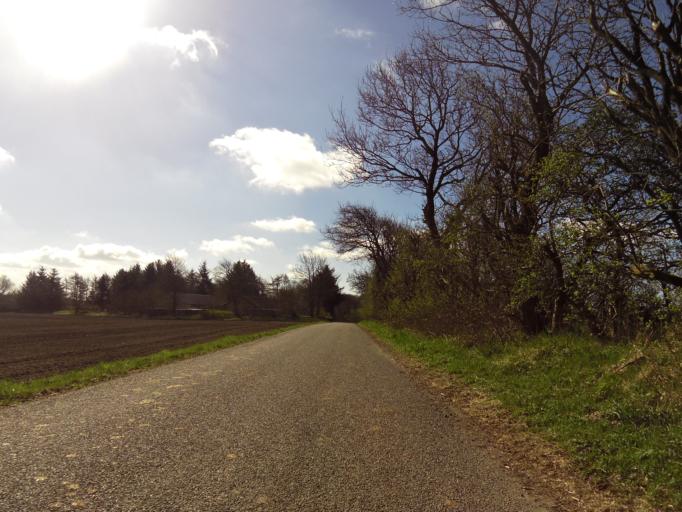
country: DK
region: Central Jutland
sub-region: Holstebro Kommune
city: Vinderup
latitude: 56.4382
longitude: 8.7248
